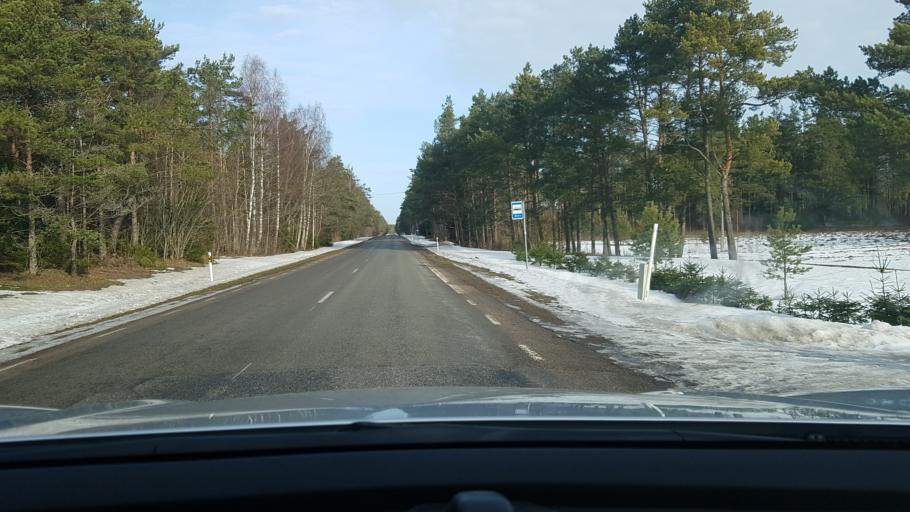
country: EE
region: Saare
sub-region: Kuressaare linn
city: Kuressaare
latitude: 58.4674
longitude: 22.7022
